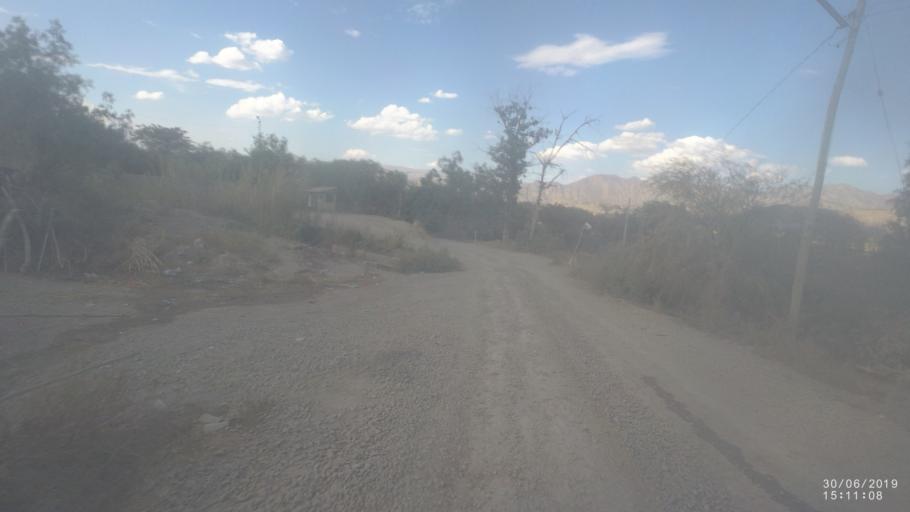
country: BO
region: Cochabamba
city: Irpa Irpa
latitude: -17.7292
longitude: -66.2934
